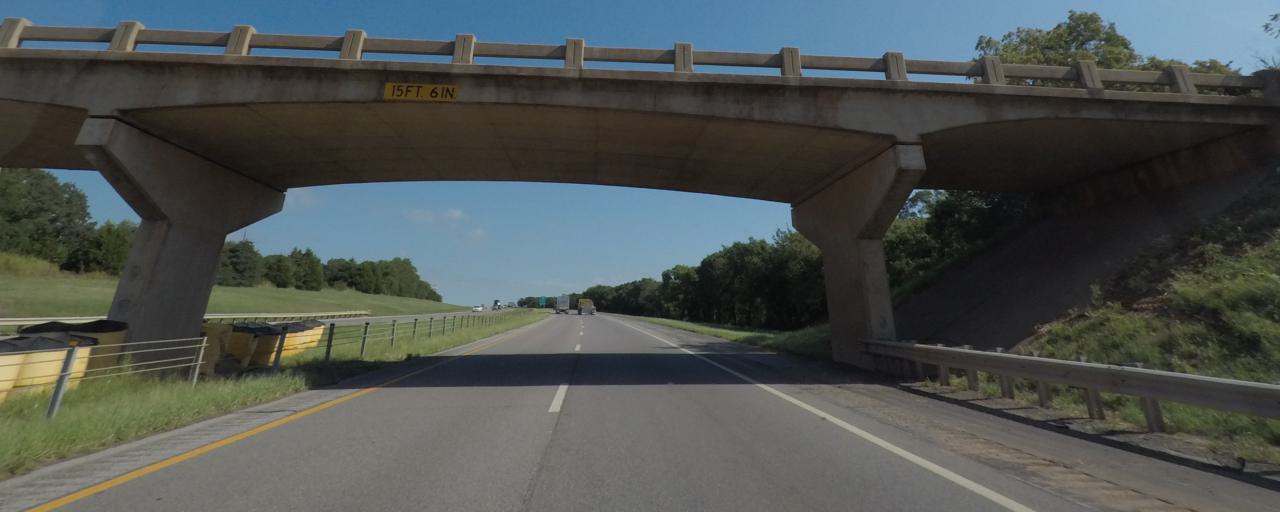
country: US
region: Oklahoma
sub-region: Logan County
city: Guthrie
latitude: 35.8417
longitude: -97.3948
